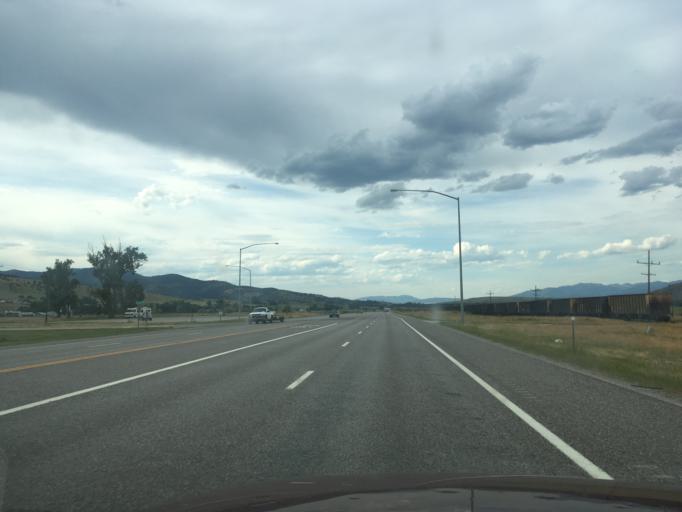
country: US
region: Montana
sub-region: Missoula County
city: Lolo
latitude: 46.7142
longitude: -114.0765
